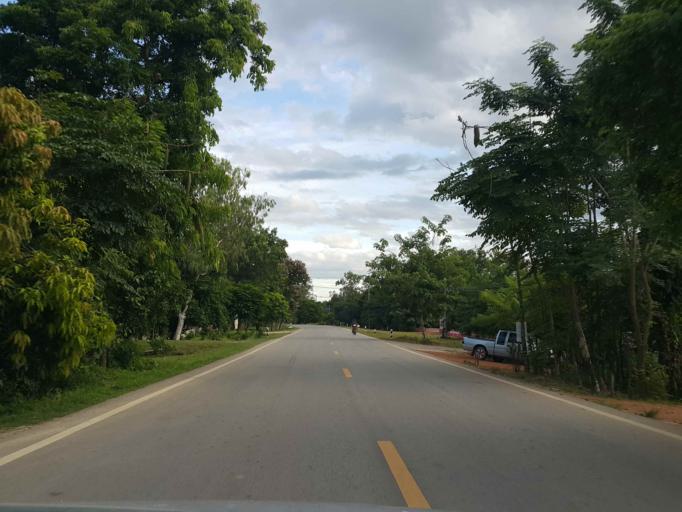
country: TH
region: Sukhothai
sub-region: Amphoe Si Satchanalai
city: Si Satchanalai
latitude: 17.5029
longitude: 99.7526
